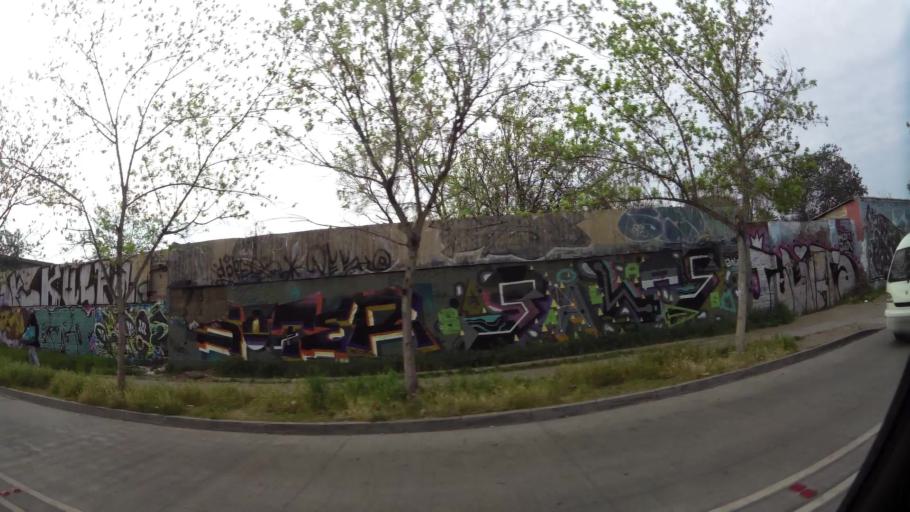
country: CL
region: Santiago Metropolitan
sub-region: Provincia de Santiago
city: Lo Prado
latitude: -33.5209
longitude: -70.7581
